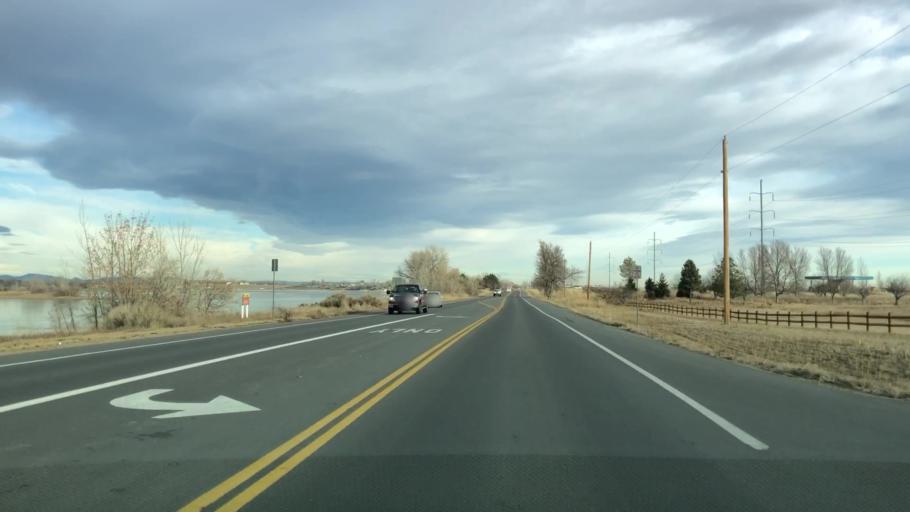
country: US
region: Colorado
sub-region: Larimer County
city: Loveland
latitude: 40.4316
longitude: -105.0454
